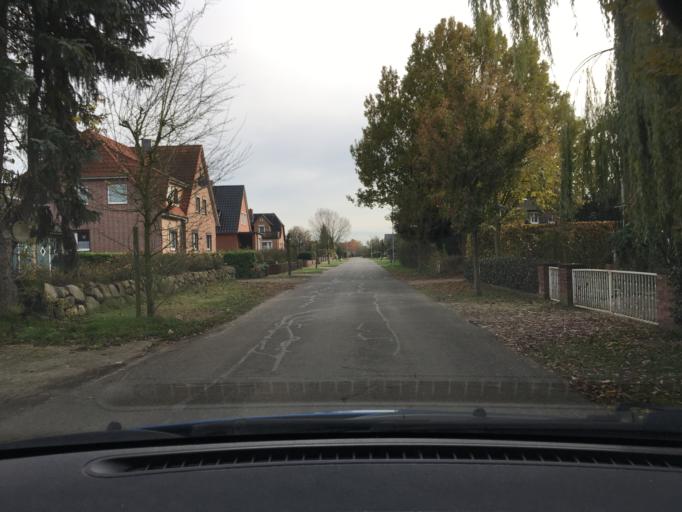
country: DE
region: Lower Saxony
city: Wittorf
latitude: 53.3281
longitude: 10.3646
